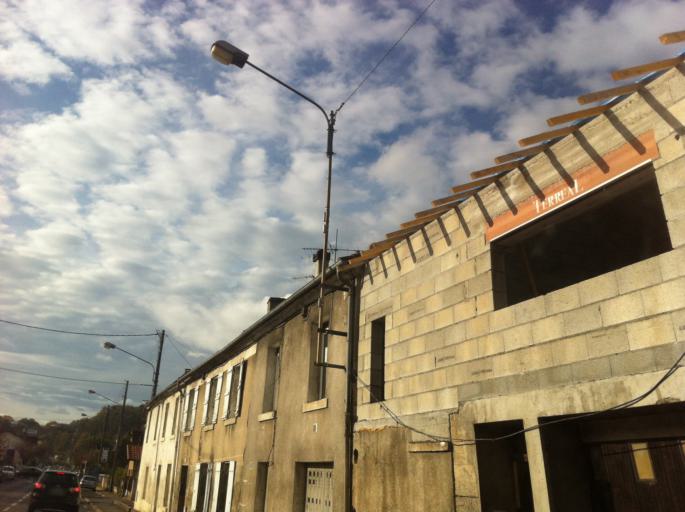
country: FR
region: Aquitaine
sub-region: Departement de la Dordogne
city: Perigueux
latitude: 45.1896
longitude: 0.7497
